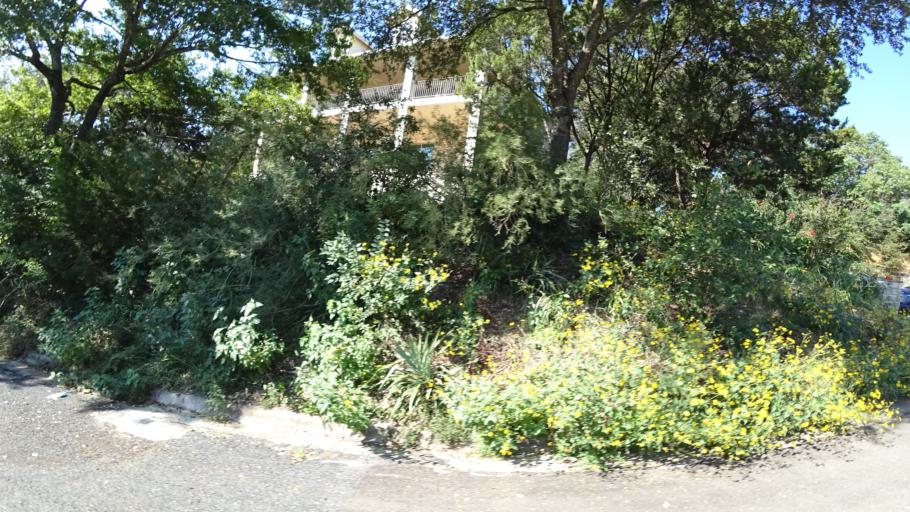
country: US
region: Texas
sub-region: Travis County
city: Rollingwood
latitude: 30.2731
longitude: -97.8067
